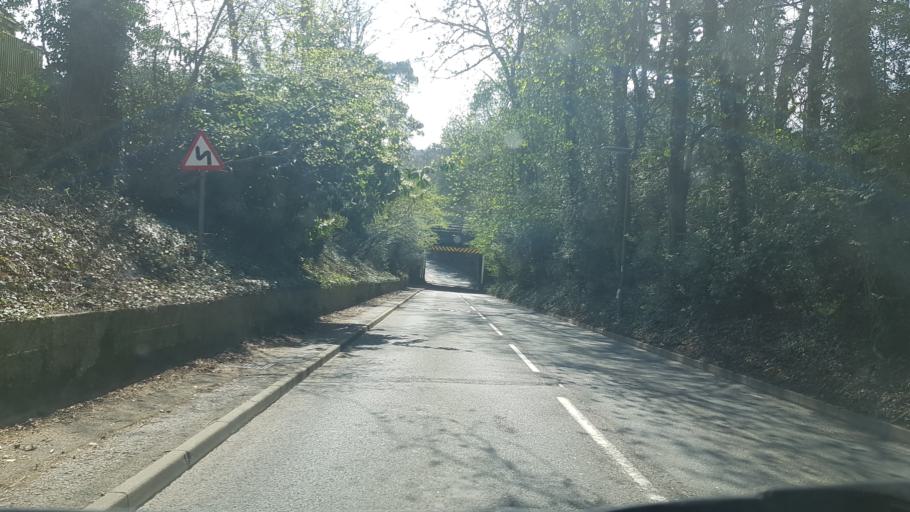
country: GB
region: England
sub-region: Surrey
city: Hindhead
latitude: 51.0864
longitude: -0.7364
